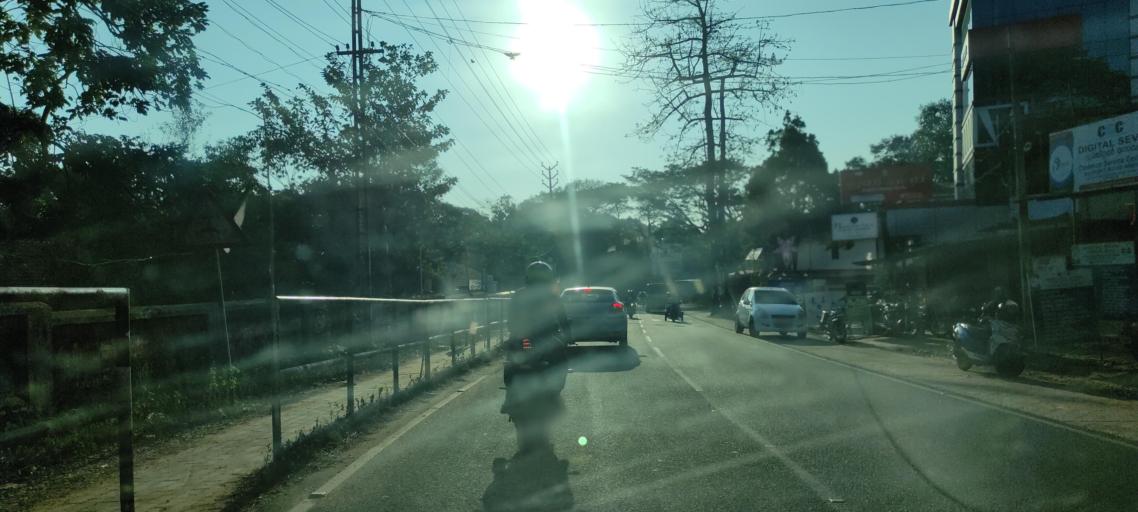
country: IN
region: Kerala
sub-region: Alappuzha
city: Kattanam
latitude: 9.1714
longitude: 76.6016
